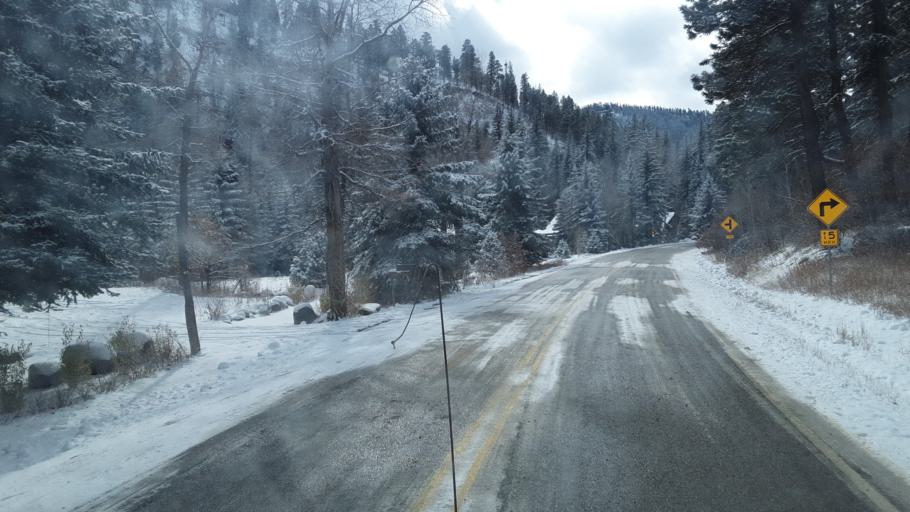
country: US
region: Colorado
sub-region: La Plata County
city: Bayfield
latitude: 37.3653
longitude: -107.6673
